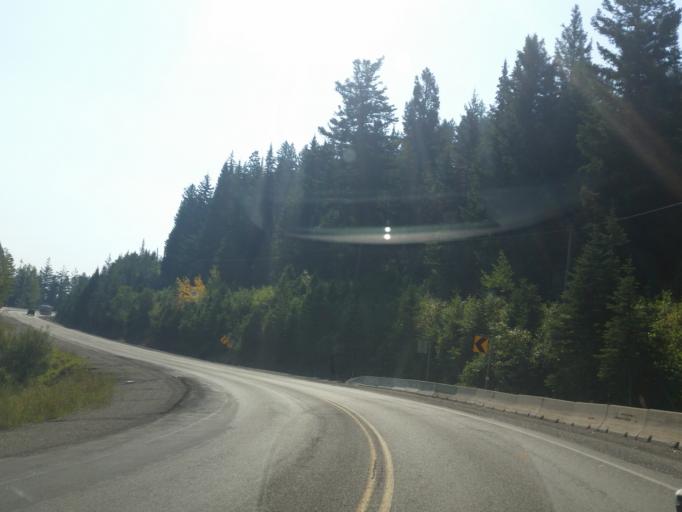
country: CA
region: British Columbia
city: Princeton
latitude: 49.2969
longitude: -120.5900
